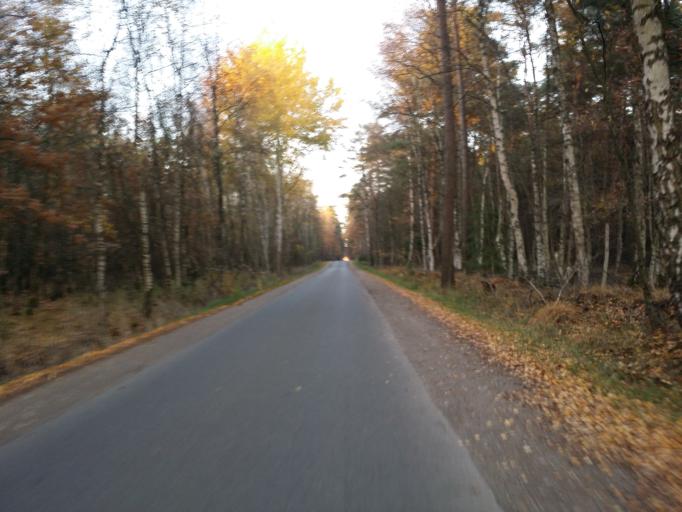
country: DE
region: Lower Saxony
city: Ahausen
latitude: 53.0897
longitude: 9.3027
